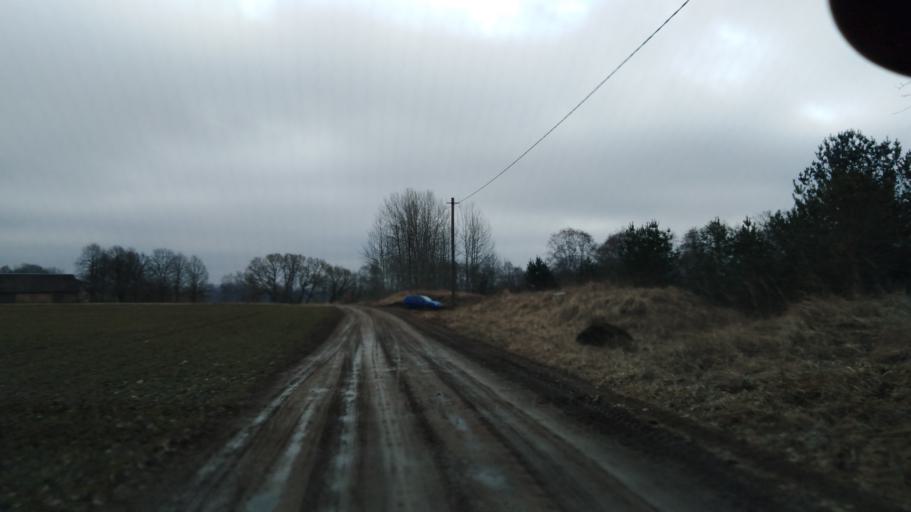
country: LV
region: Kuldigas Rajons
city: Kuldiga
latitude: 56.9845
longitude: 21.9624
